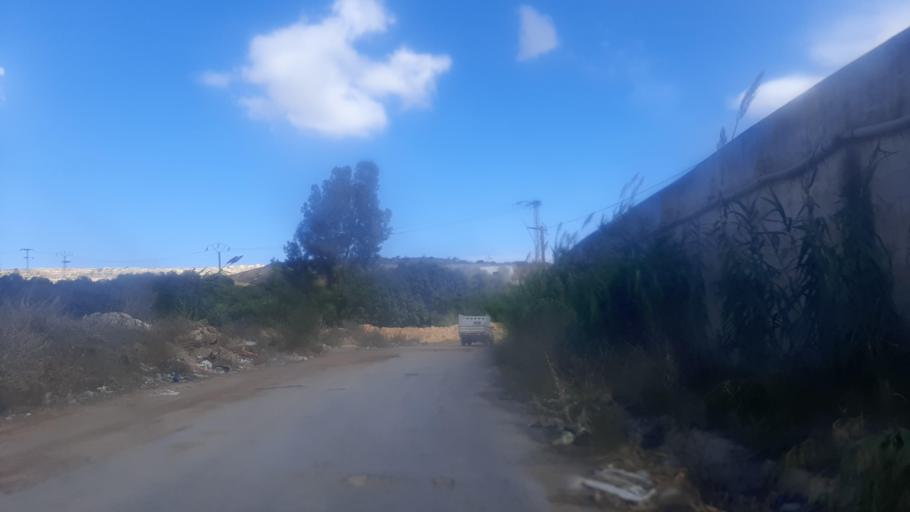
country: TN
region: Nabul
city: Nabeul
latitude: 36.4898
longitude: 10.7001
